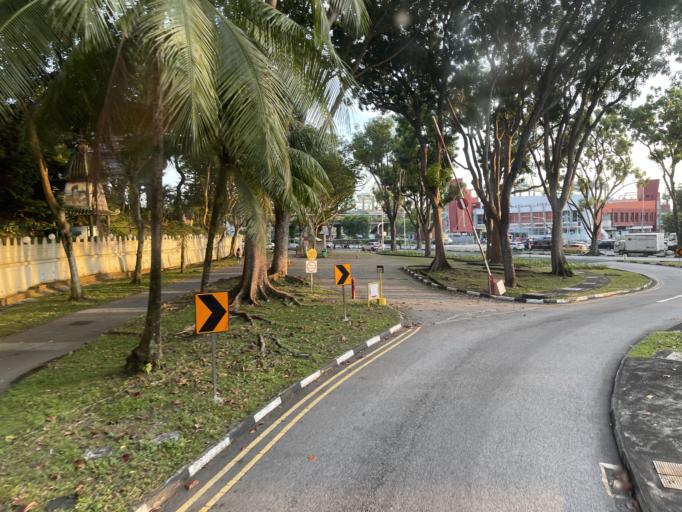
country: SG
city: Singapore
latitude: 1.2847
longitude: 103.7811
